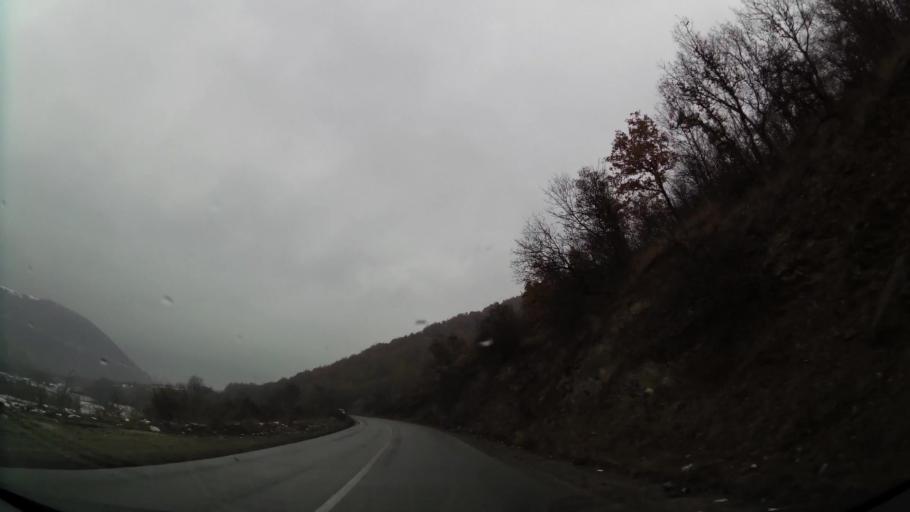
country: XK
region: Ferizaj
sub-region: Hani i Elezit
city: Hani i Elezit
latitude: 42.1317
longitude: 21.3124
